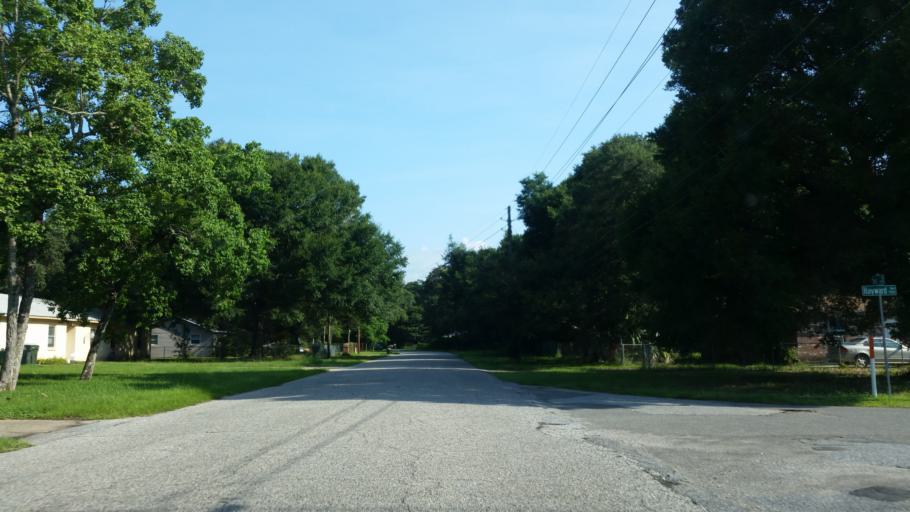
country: US
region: Florida
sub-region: Escambia County
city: Bellview
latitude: 30.4417
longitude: -87.3151
